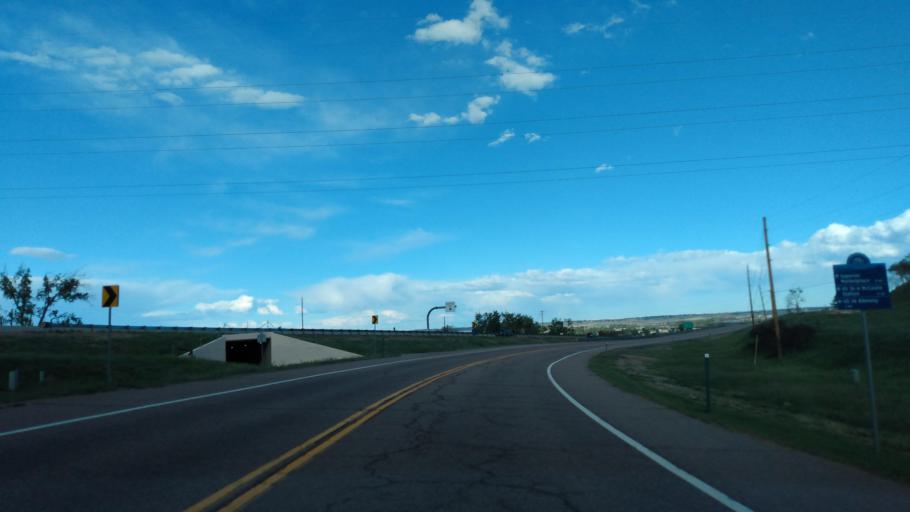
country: US
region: Colorado
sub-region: Boulder County
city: Superior
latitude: 39.9635
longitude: -105.1826
